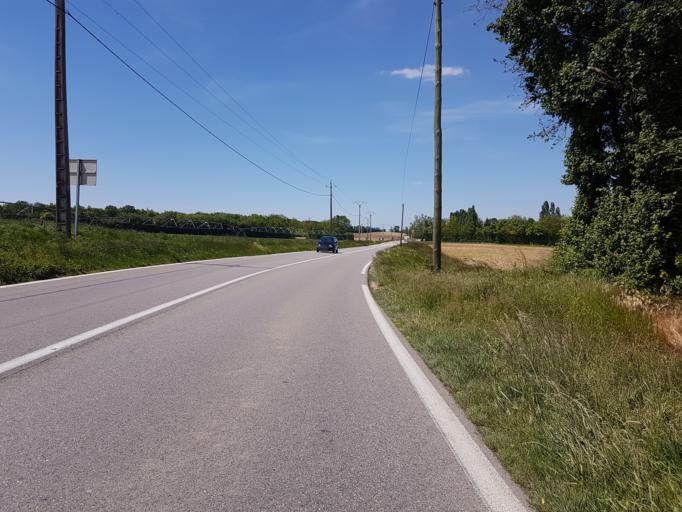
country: FR
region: Rhone-Alpes
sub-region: Departement de l'Isere
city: Chavanoz
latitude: 45.7849
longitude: 5.1497
